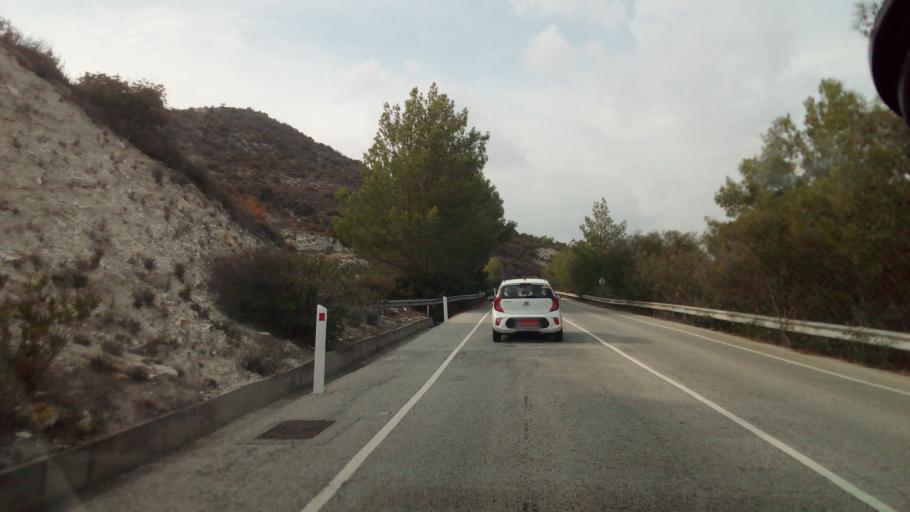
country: CY
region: Larnaka
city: Kofinou
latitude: 34.8341
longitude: 33.3498
